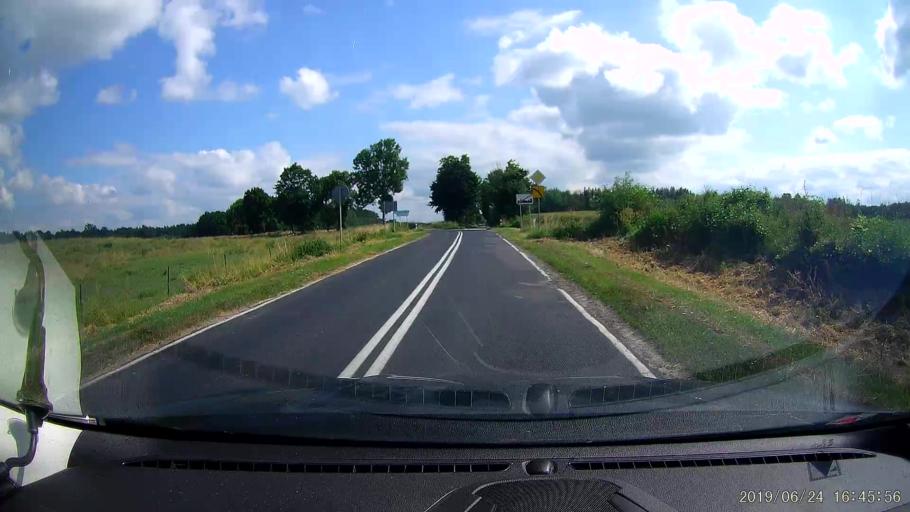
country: PL
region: Lublin Voivodeship
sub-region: Powiat tomaszowski
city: Laszczow
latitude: 50.5306
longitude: 23.6726
